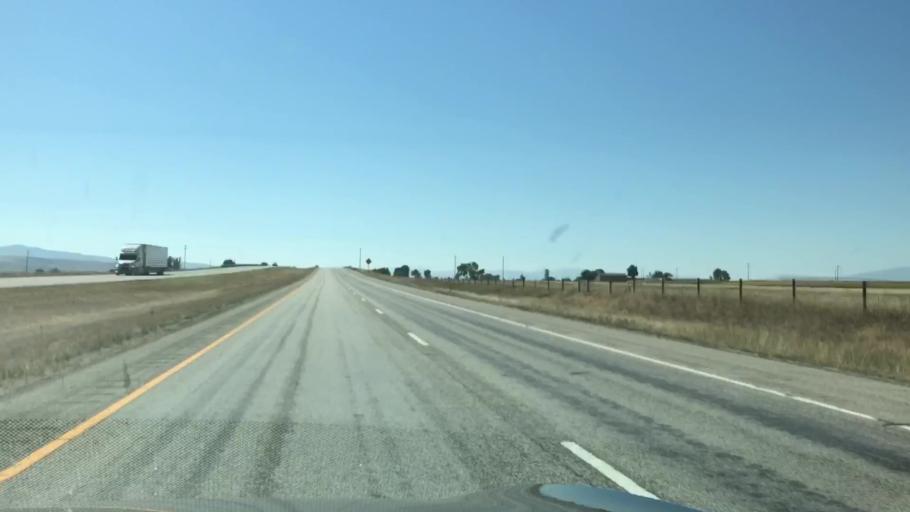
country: US
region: Montana
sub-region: Powell County
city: Deer Lodge
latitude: 46.3212
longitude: -112.7452
